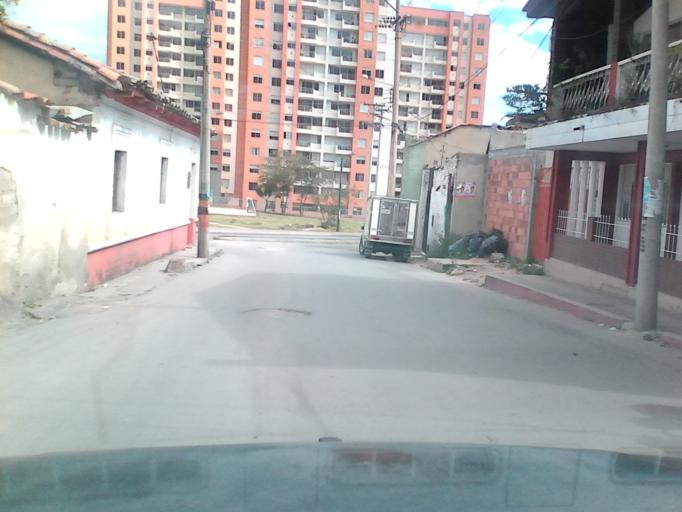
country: CO
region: Boyaca
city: Duitama
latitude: 5.8340
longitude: -73.0334
